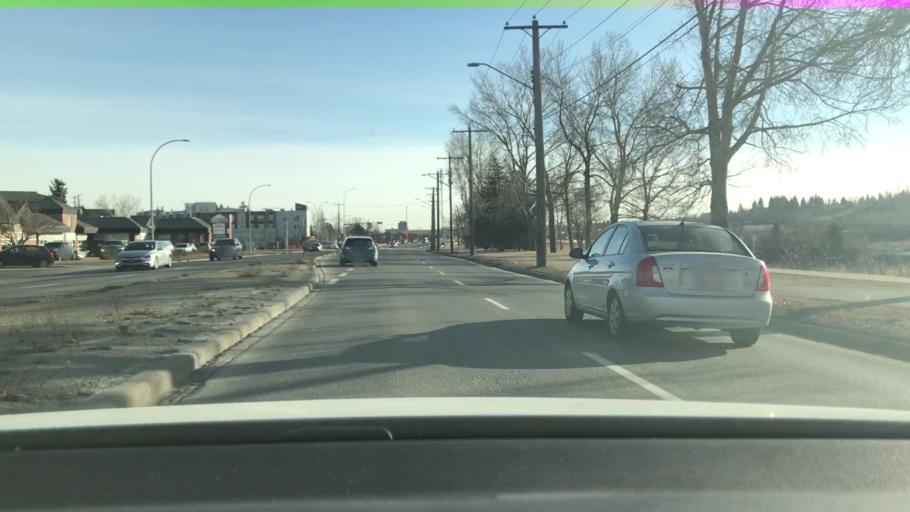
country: CA
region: Alberta
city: Calgary
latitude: 51.0534
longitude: -114.1237
